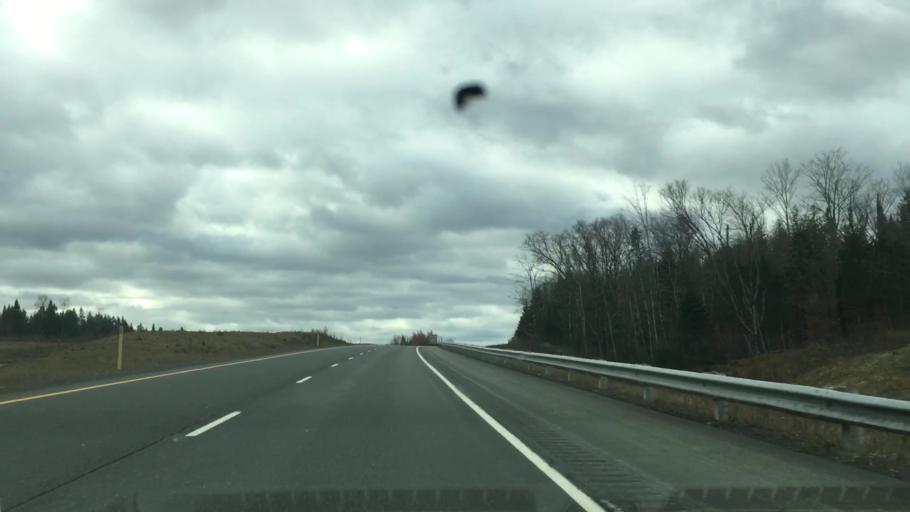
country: US
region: Maine
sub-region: Aroostook County
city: Fort Fairfield
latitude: 46.6601
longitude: -67.7330
